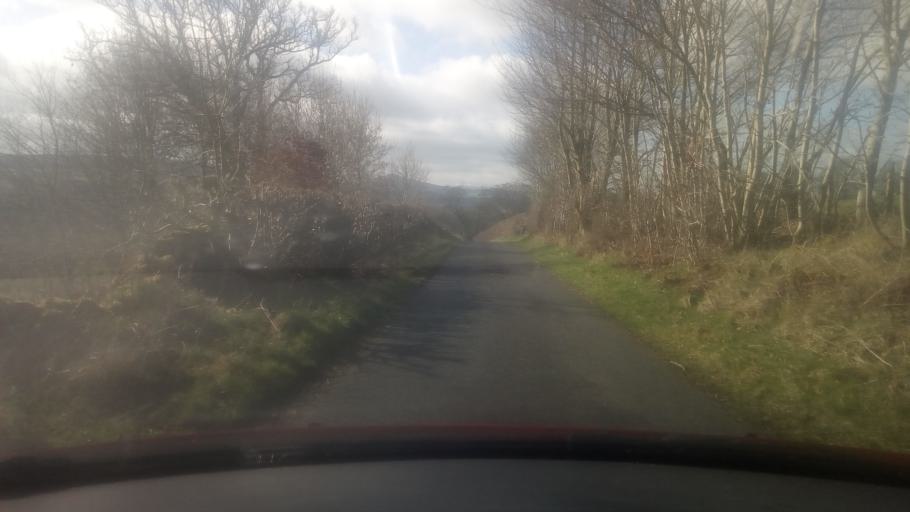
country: GB
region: Scotland
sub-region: The Scottish Borders
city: Jedburgh
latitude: 55.5219
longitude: -2.5769
